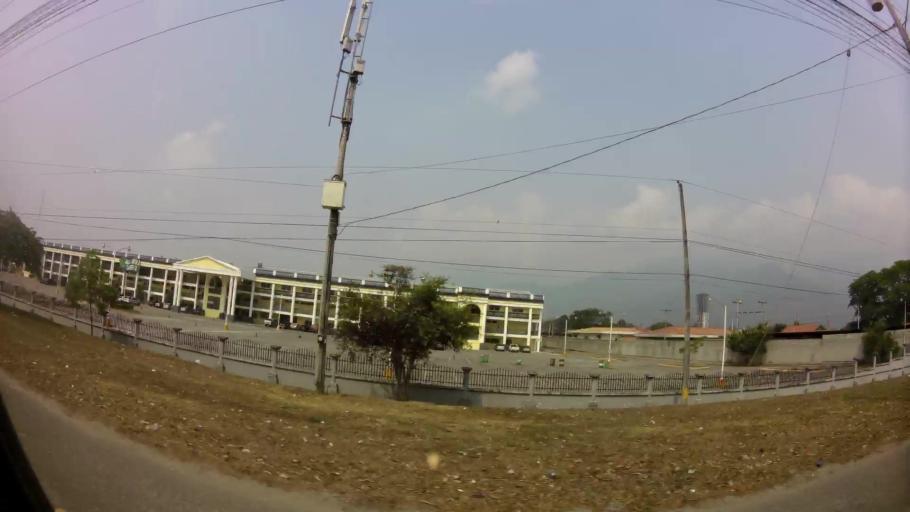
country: HN
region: Cortes
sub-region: San Pedro Sula
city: Pena Blanca
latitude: 15.5524
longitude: -88.0119
